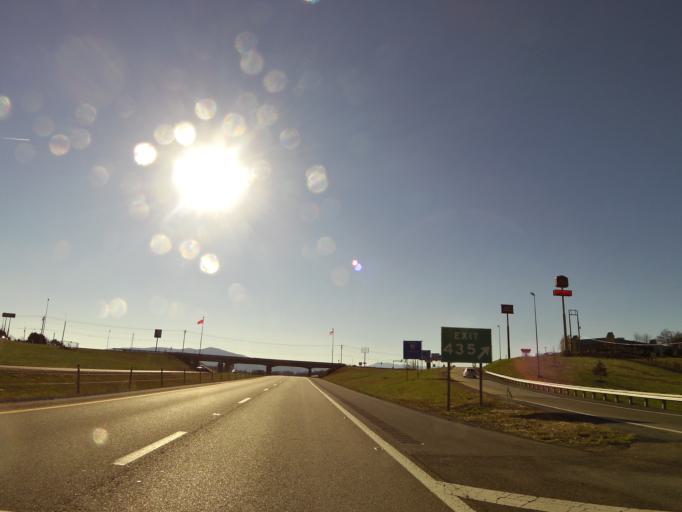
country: US
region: Tennessee
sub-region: Cocke County
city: Newport
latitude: 35.9502
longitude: -83.2045
